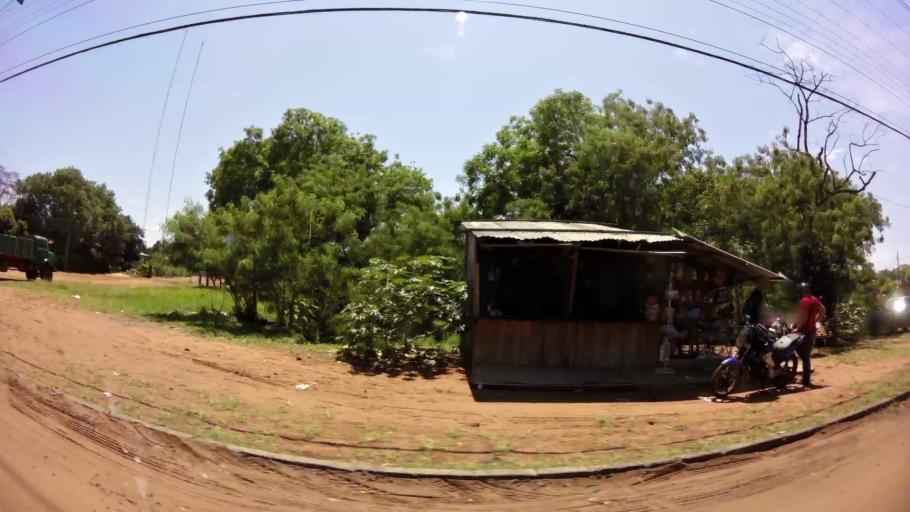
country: PY
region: Central
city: Nemby
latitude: -25.3982
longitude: -57.5350
